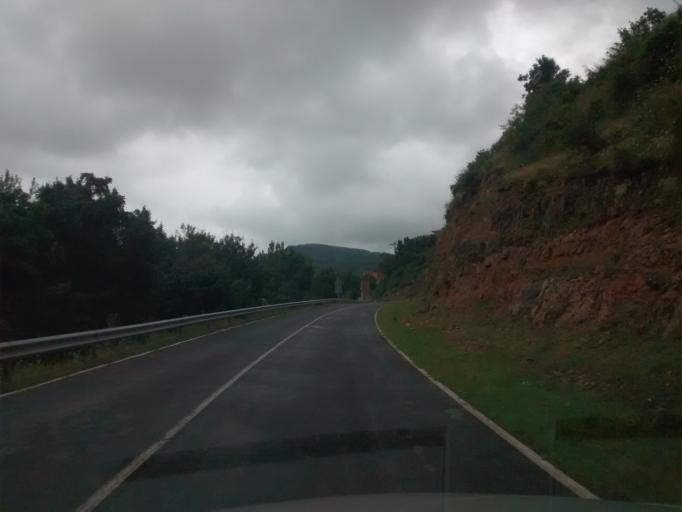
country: ES
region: La Rioja
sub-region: Provincia de La Rioja
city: Ajamil
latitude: 42.1705
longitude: -2.4852
